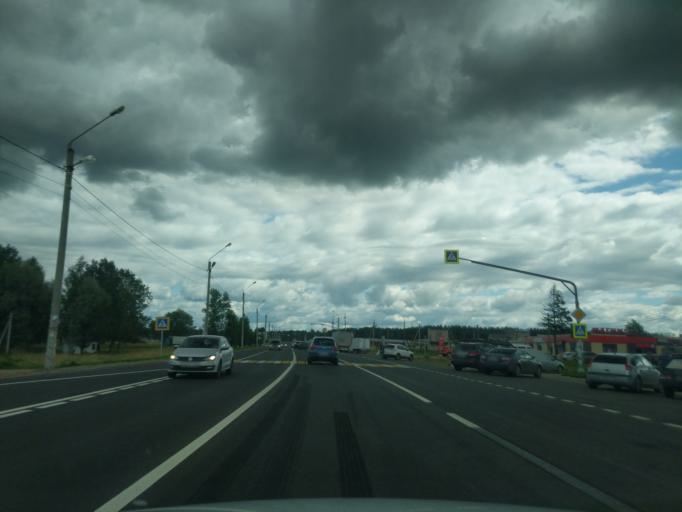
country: RU
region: Jaroslavl
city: Tunoshna
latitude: 57.5410
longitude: 40.1218
